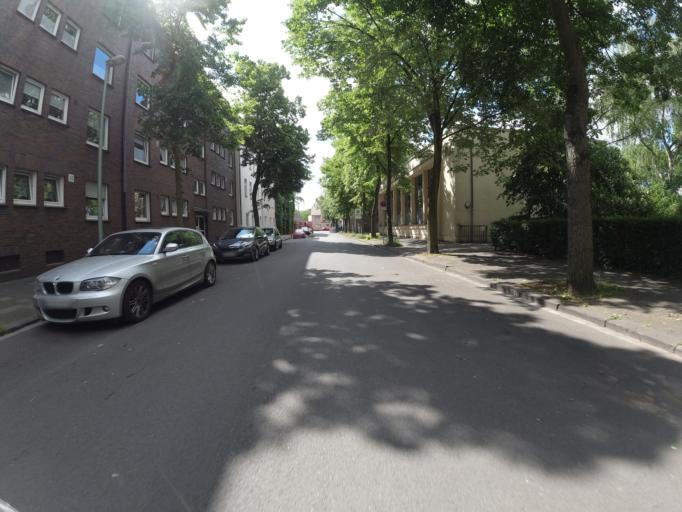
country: DE
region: North Rhine-Westphalia
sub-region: Regierungsbezirk Dusseldorf
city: Hochfeld
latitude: 51.3962
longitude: 6.6952
